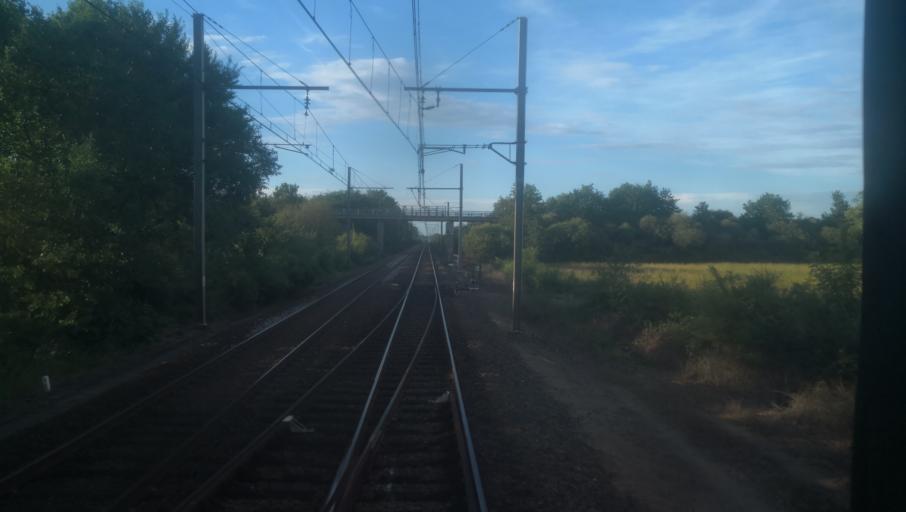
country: FR
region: Centre
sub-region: Departement de l'Indre
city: Luant
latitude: 46.6972
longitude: 1.5646
